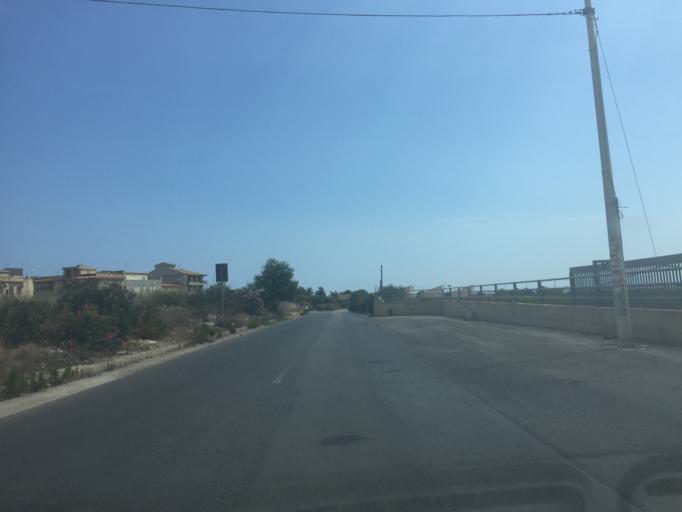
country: IT
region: Sicily
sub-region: Ragusa
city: Santa Croce Camerina
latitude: 36.8257
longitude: 14.5188
